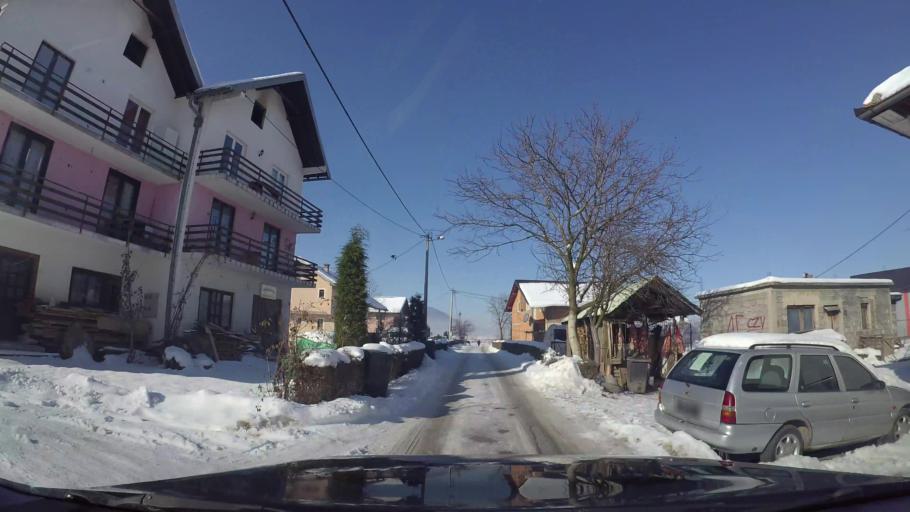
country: BA
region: Federation of Bosnia and Herzegovina
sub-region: Kanton Sarajevo
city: Sarajevo
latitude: 43.7998
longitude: 18.3455
